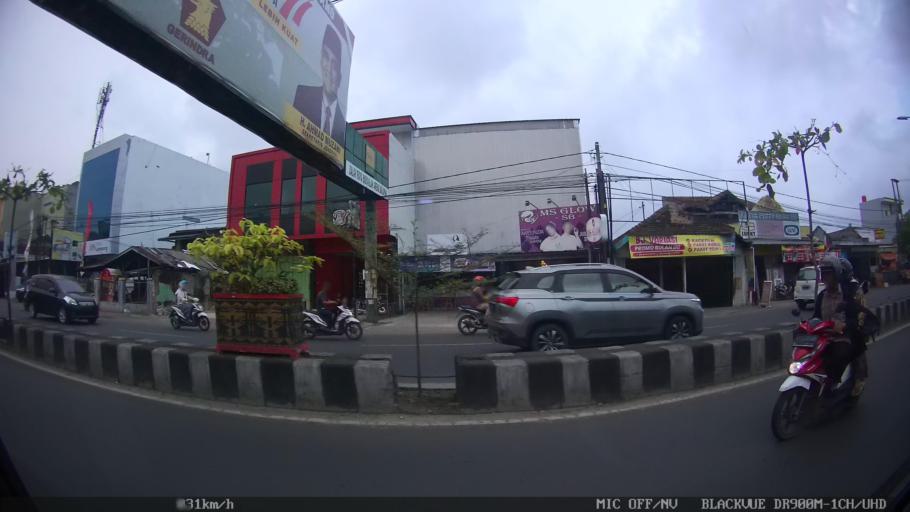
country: ID
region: Lampung
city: Bandarlampung
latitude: -5.4076
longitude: 105.2711
